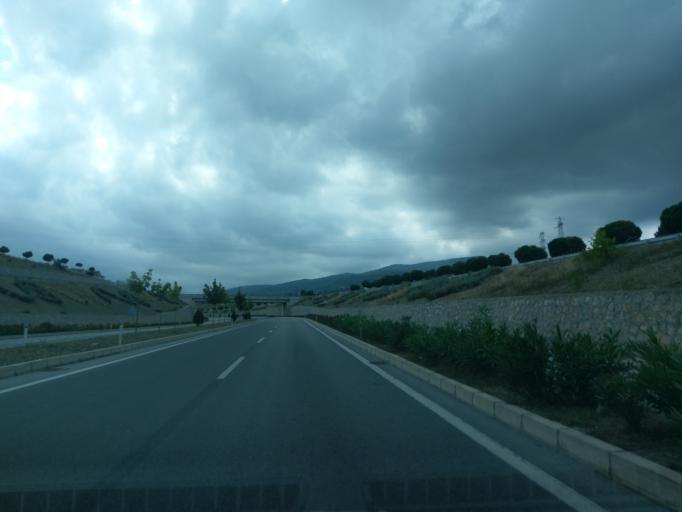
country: TR
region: Sinop
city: Gerze
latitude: 41.8139
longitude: 35.1676
